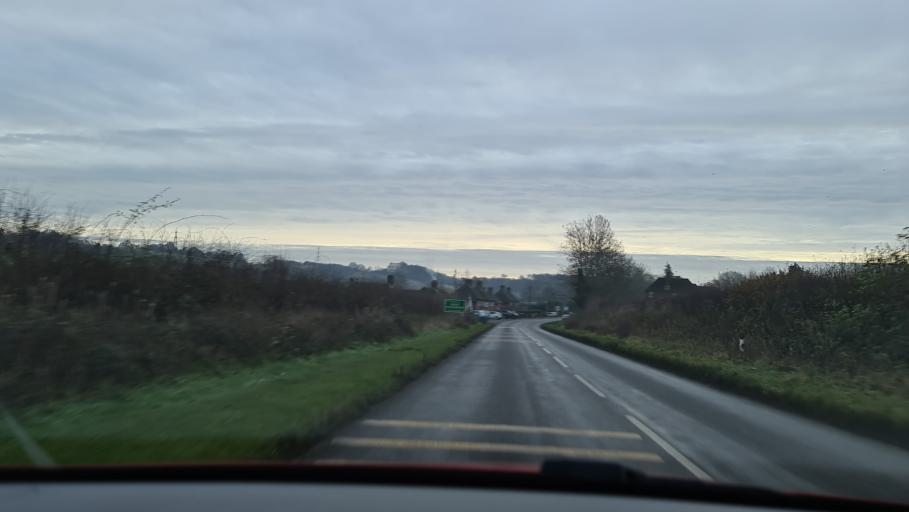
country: GB
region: England
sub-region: Buckinghamshire
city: Great Missenden
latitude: 51.7078
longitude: -0.7173
